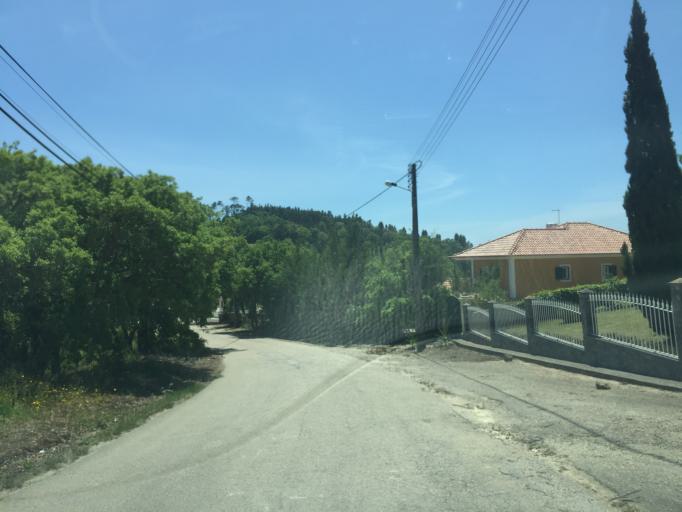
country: PT
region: Lisbon
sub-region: Mafra
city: Venda do Pinheiro
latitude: 38.8942
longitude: -9.2294
